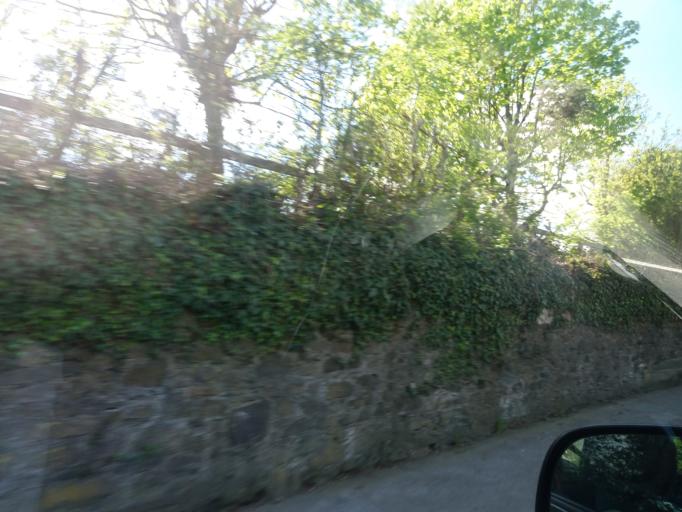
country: IE
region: Munster
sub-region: Waterford
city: Waterford
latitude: 52.2462
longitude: -7.0752
